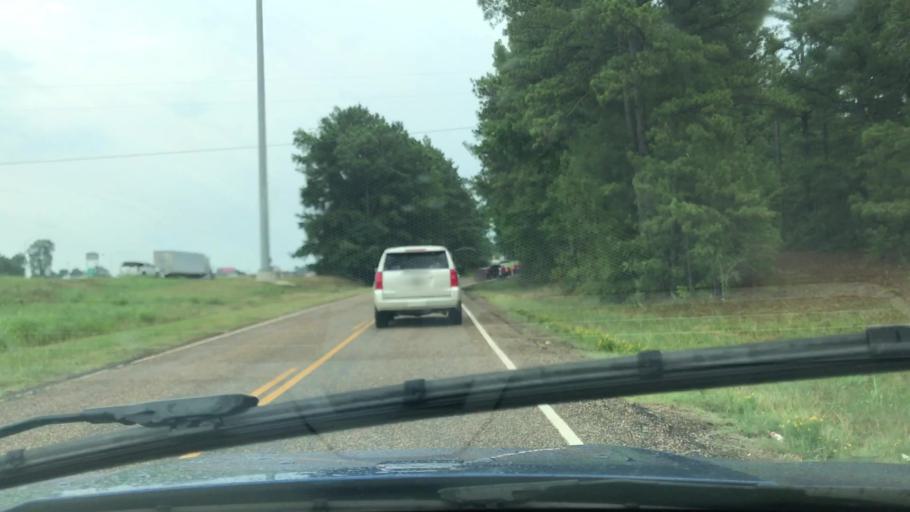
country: US
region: Texas
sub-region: Harrison County
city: Waskom
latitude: 32.4794
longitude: -94.0920
